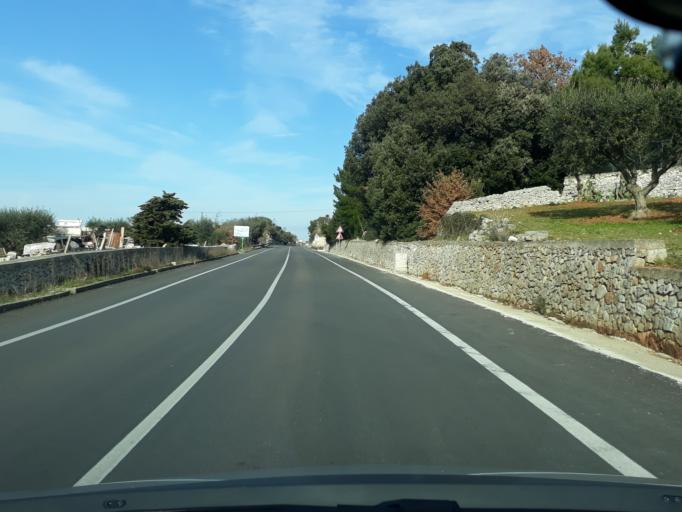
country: IT
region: Apulia
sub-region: Provincia di Bari
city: Locorotondo
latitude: 40.7808
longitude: 17.3388
